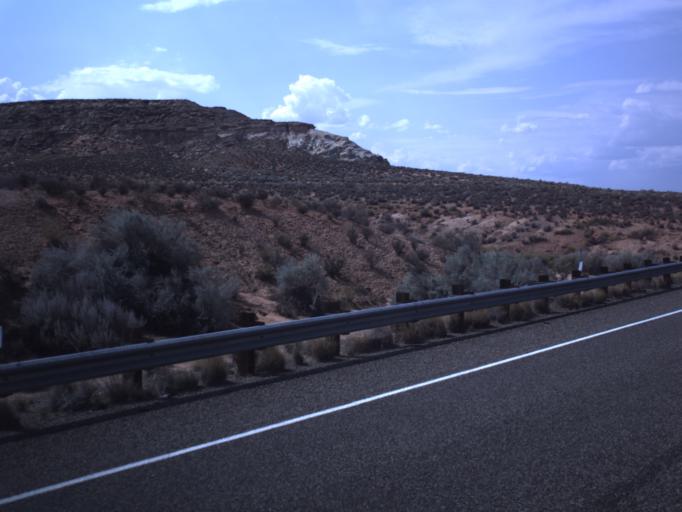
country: US
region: Arizona
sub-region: Coconino County
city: Page
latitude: 37.0467
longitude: -111.6231
